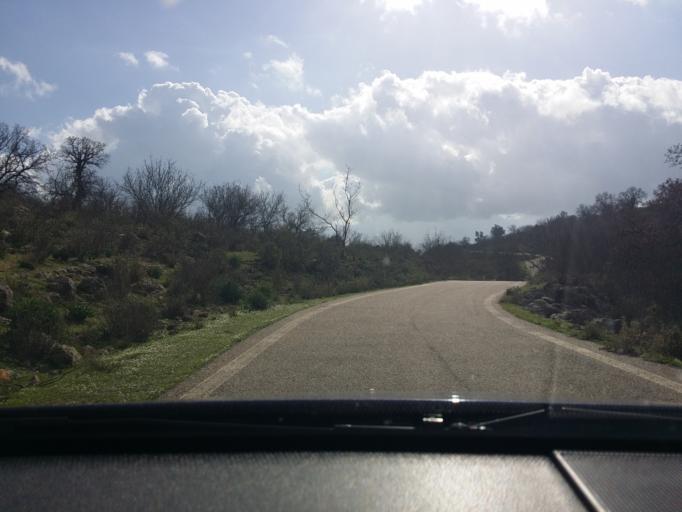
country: GR
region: West Greece
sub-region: Nomos Aitolias kai Akarnanias
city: Fitiai
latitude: 38.6416
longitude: 21.1958
